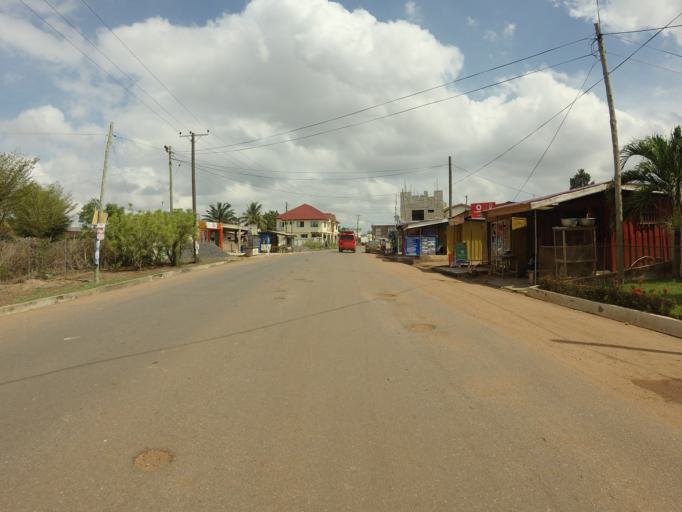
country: GH
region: Greater Accra
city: Nungua
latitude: 5.6262
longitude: -0.0927
